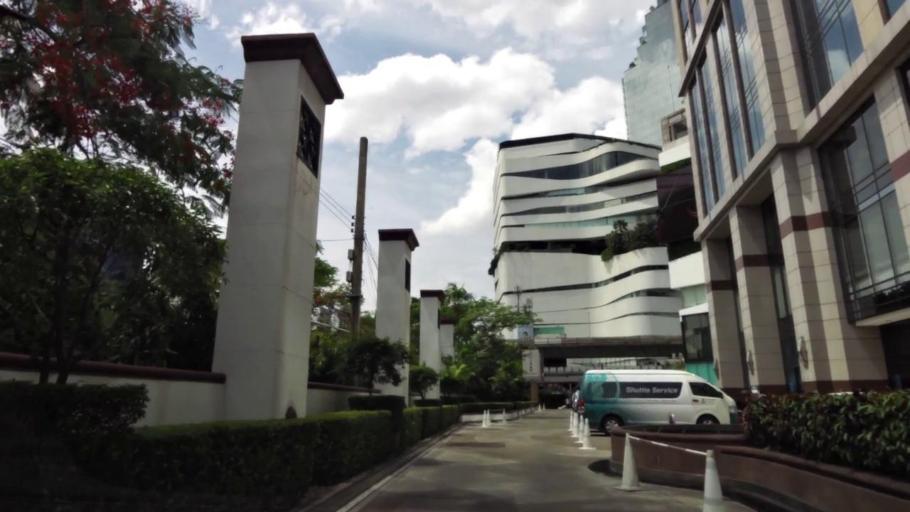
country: TH
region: Bangkok
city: Khlong Toei
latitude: 13.7302
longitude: 100.5681
